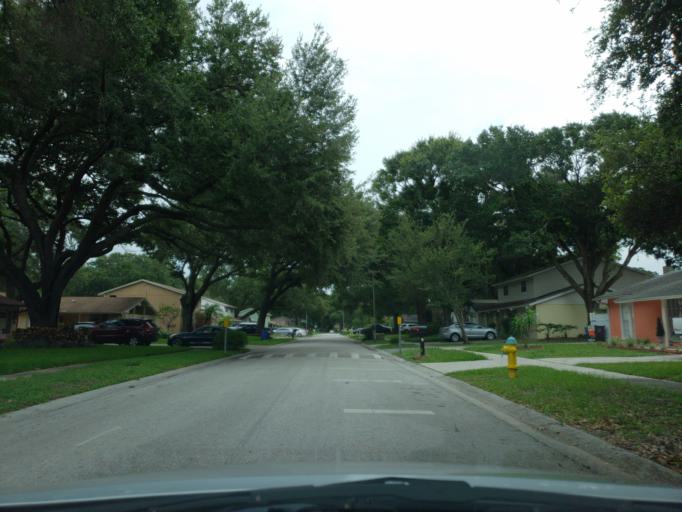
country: US
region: Florida
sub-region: Hillsborough County
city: Egypt Lake-Leto
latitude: 28.0023
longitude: -82.4955
